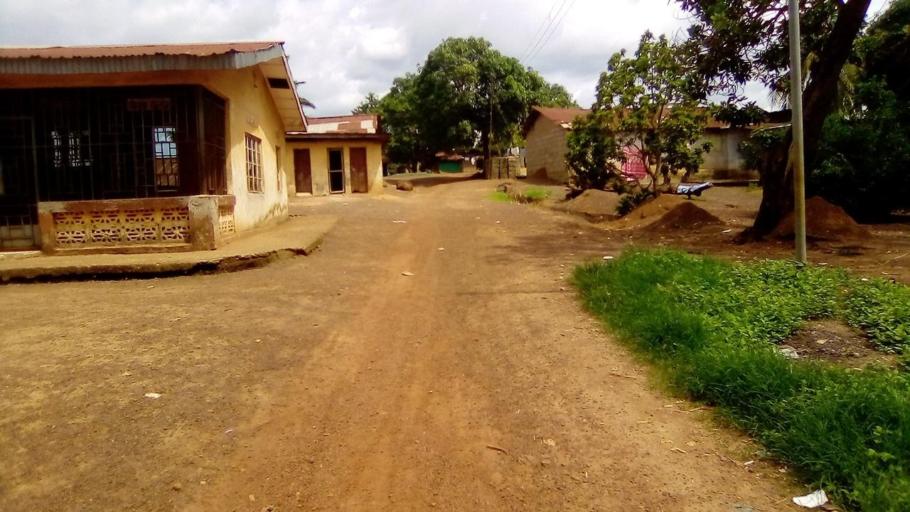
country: SL
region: Southern Province
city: Bo
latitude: 7.9631
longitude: -11.7224
